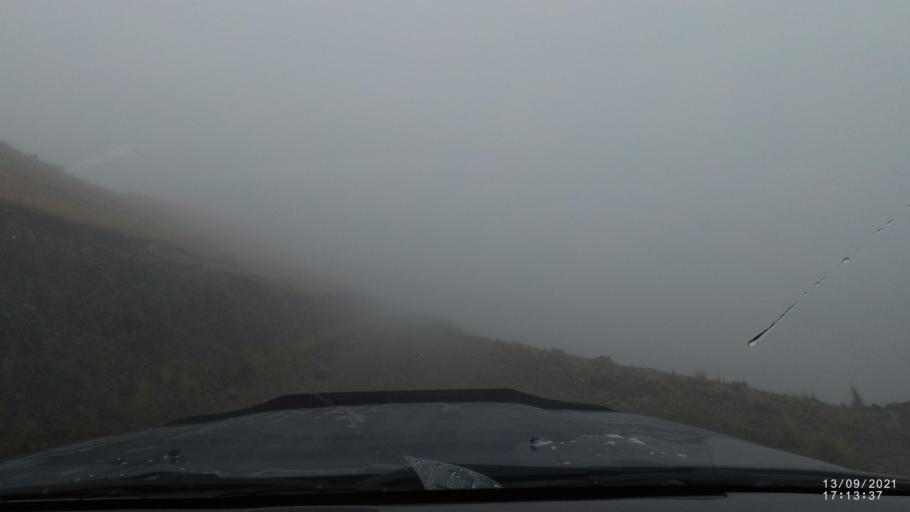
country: BO
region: Cochabamba
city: Colomi
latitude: -17.3402
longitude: -65.7504
